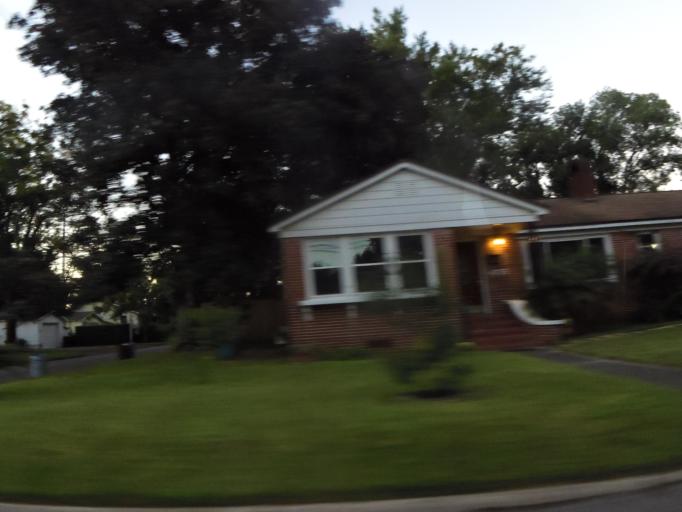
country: US
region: Florida
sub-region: Duval County
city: Jacksonville
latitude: 30.3153
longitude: -81.7284
